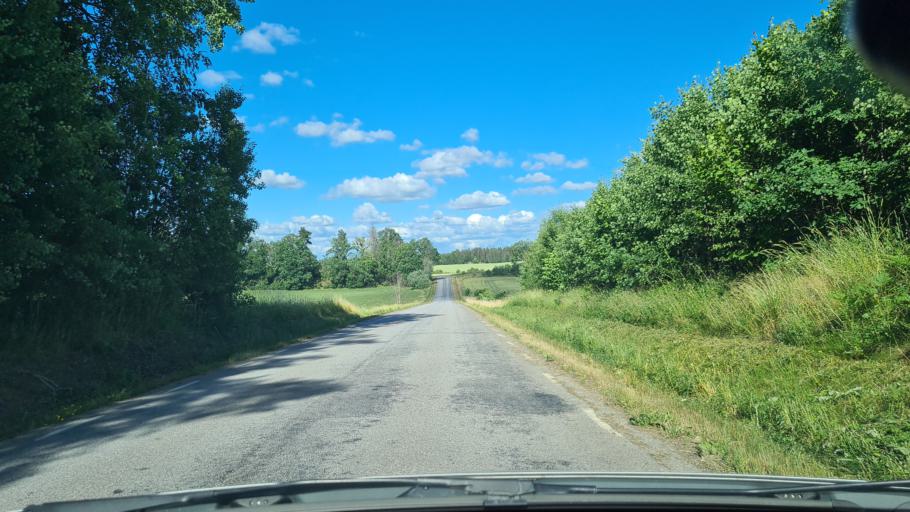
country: SE
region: Soedermanland
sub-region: Nykopings Kommun
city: Olstorp
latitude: 58.8222
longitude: 16.4987
